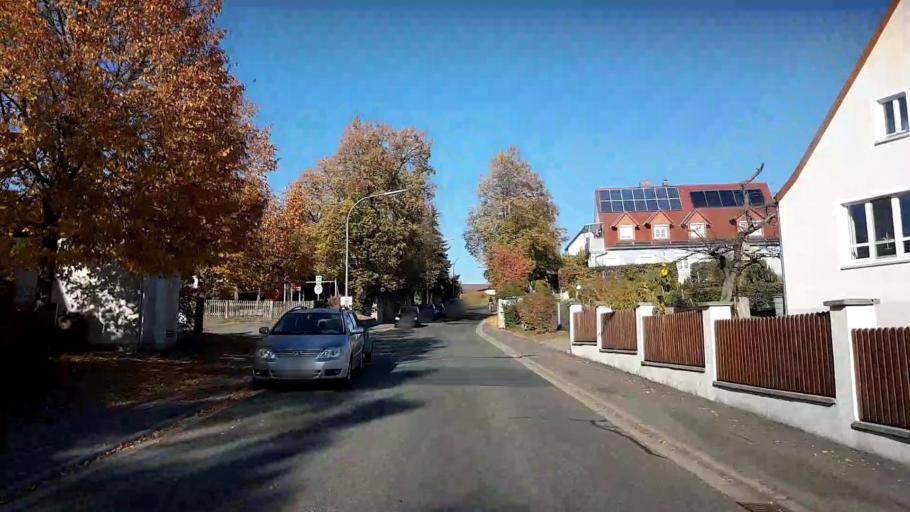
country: DE
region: Bavaria
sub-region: Upper Franconia
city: Walsdorf
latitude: 49.8713
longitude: 10.7833
